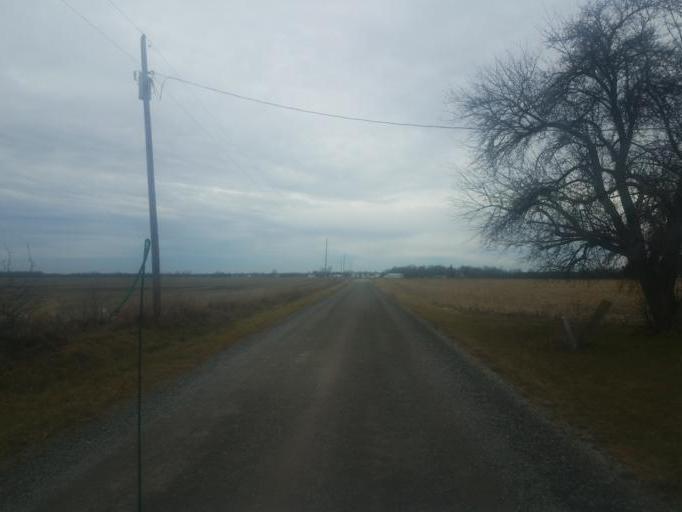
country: US
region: Ohio
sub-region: Morrow County
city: Mount Gilead
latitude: 40.6270
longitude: -82.9151
